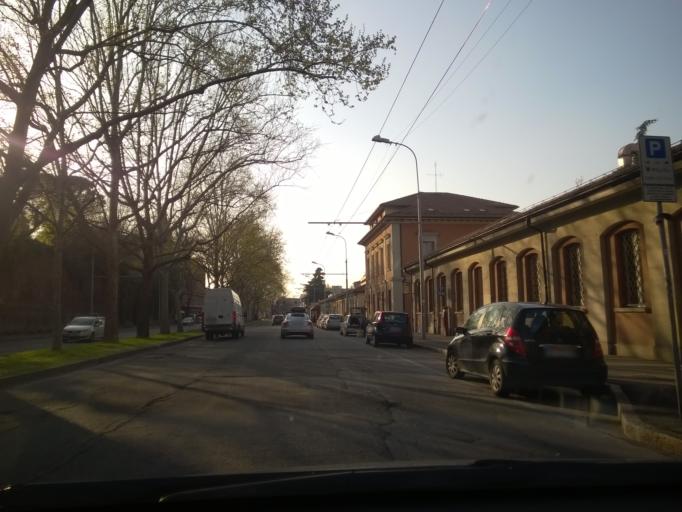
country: IT
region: Emilia-Romagna
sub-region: Provincia di Bologna
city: Bologna
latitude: 44.5015
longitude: 11.3552
